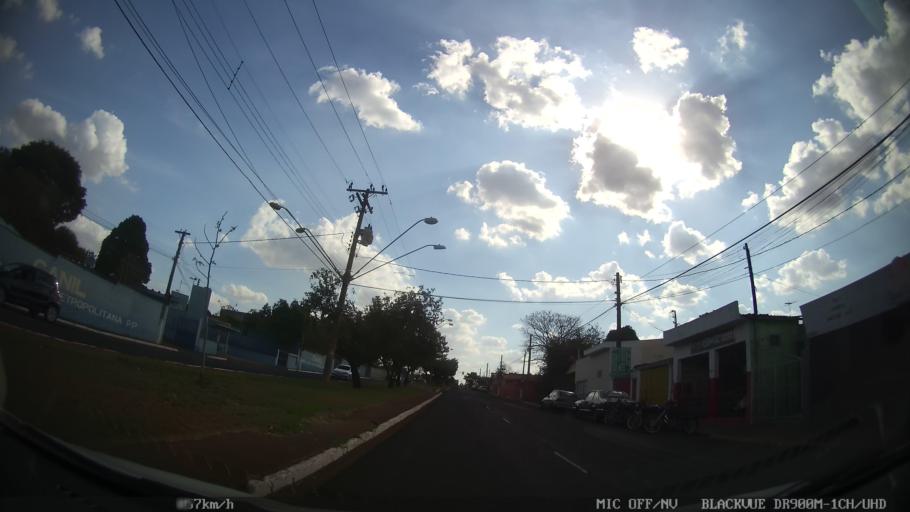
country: BR
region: Sao Paulo
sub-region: Ribeirao Preto
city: Ribeirao Preto
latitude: -21.1877
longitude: -47.8311
